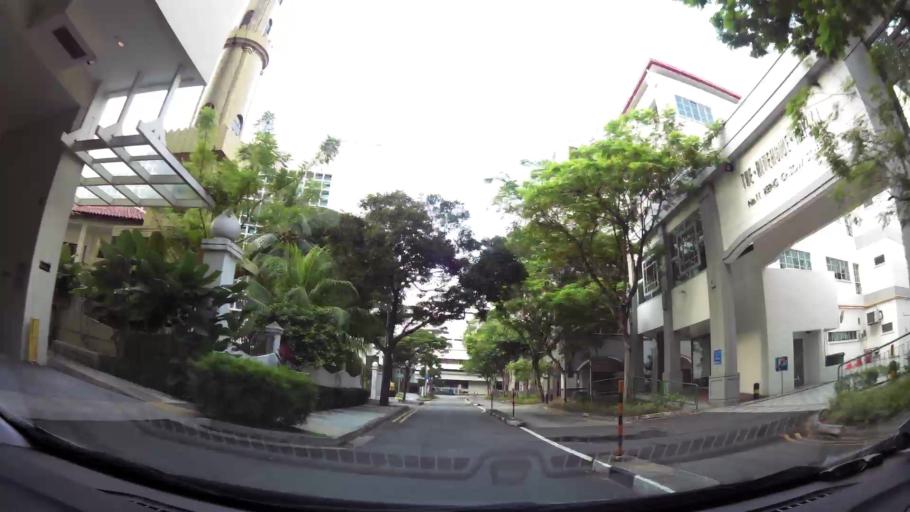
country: SG
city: Singapore
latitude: 1.2883
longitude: 103.8441
